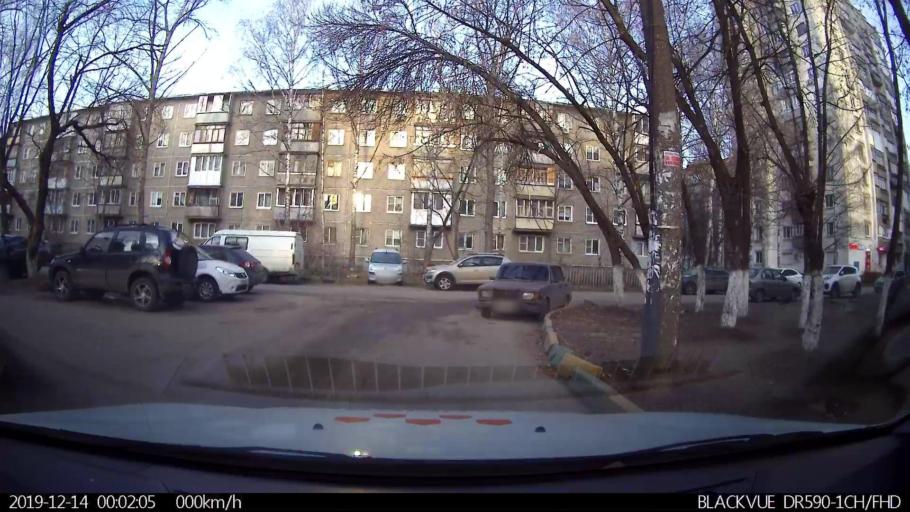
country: RU
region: Nizjnij Novgorod
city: Nizhniy Novgorod
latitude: 56.2732
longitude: 43.9153
